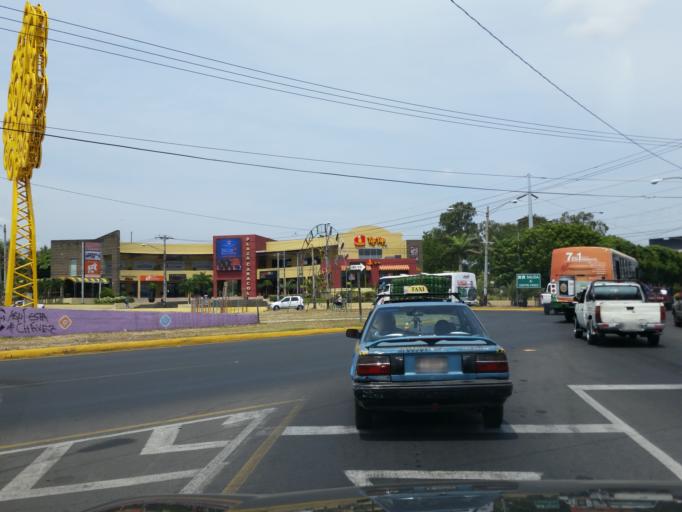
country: NI
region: Managua
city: Managua
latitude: 12.1259
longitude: -86.2832
